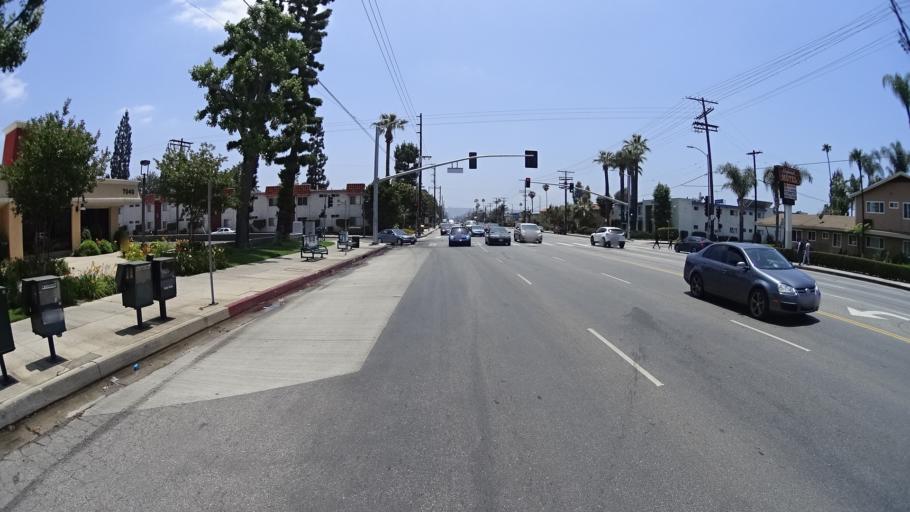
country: US
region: California
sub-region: Los Angeles County
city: Van Nuys
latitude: 34.1989
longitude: -118.4661
